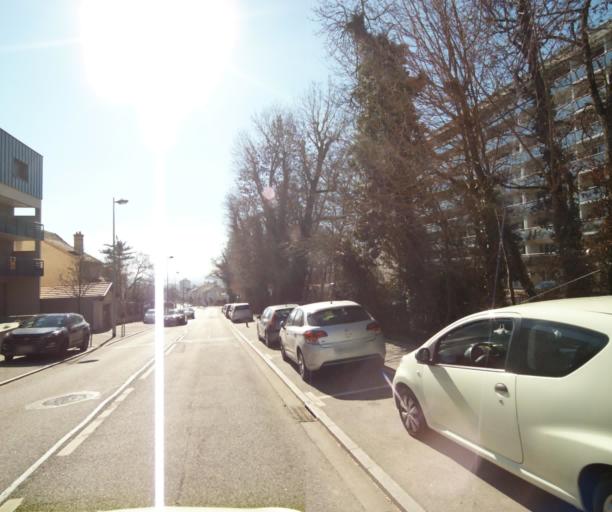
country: FR
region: Lorraine
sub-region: Departement de Meurthe-et-Moselle
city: Saint-Max
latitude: 48.7102
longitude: 6.2042
